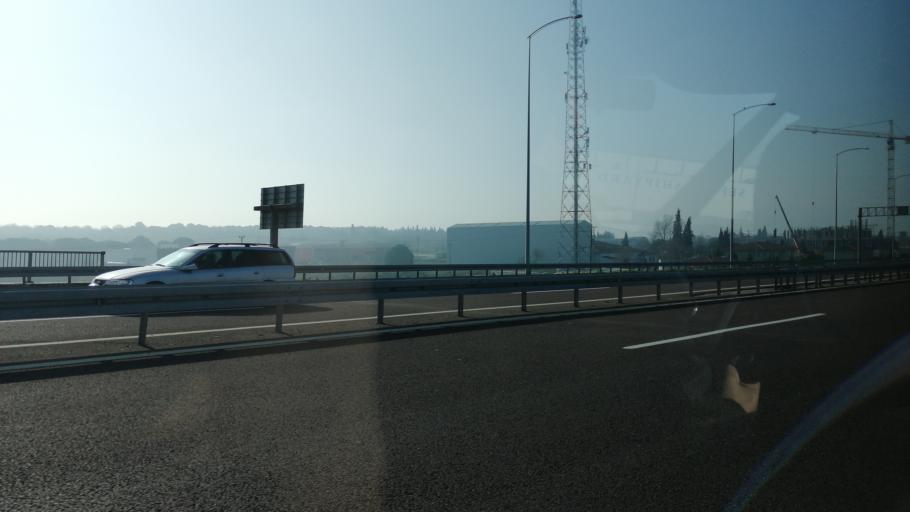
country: TR
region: Yalova
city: Altinova
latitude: 40.7305
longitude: 29.5074
